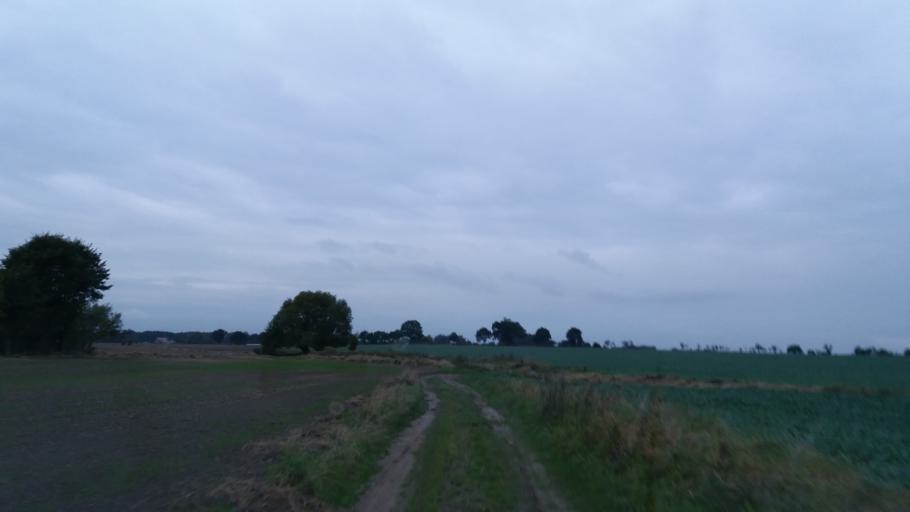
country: PL
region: West Pomeranian Voivodeship
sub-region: Powiat choszczenski
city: Krzecin
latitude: 53.0839
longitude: 15.4101
